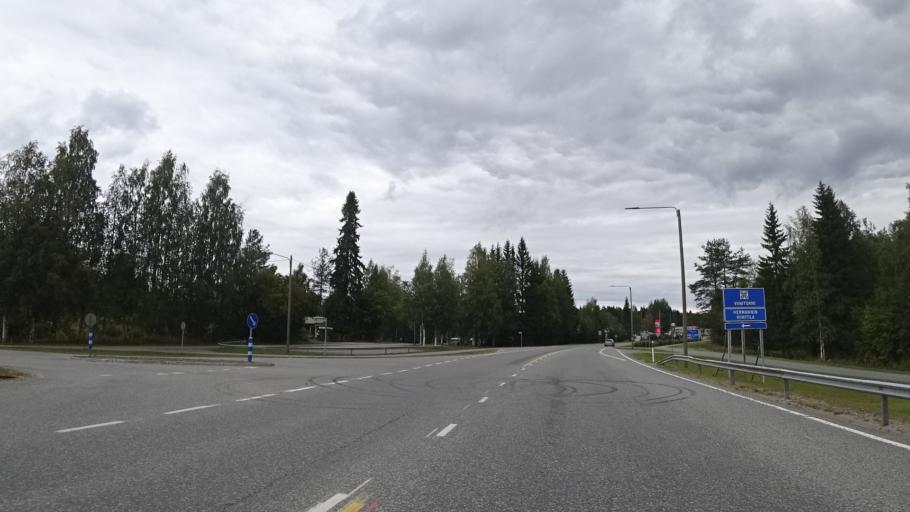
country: FI
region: North Karelia
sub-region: Joensuu
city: Ilomantsi
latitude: 62.6655
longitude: 30.9365
